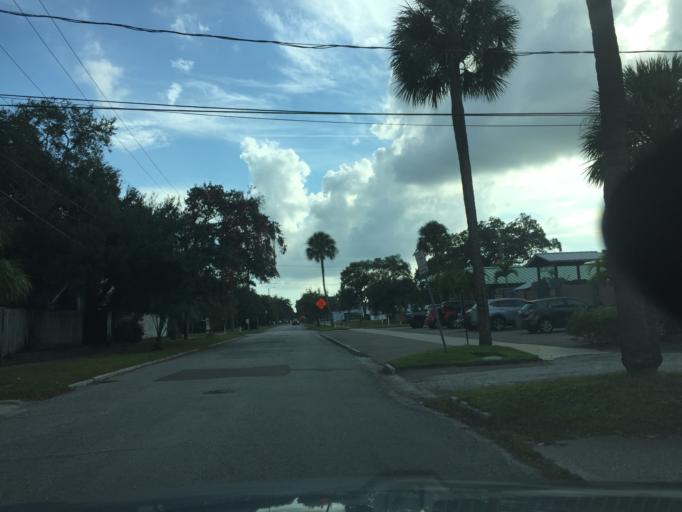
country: US
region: Florida
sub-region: Hillsborough County
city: Tampa
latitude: 27.9465
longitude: -82.4789
